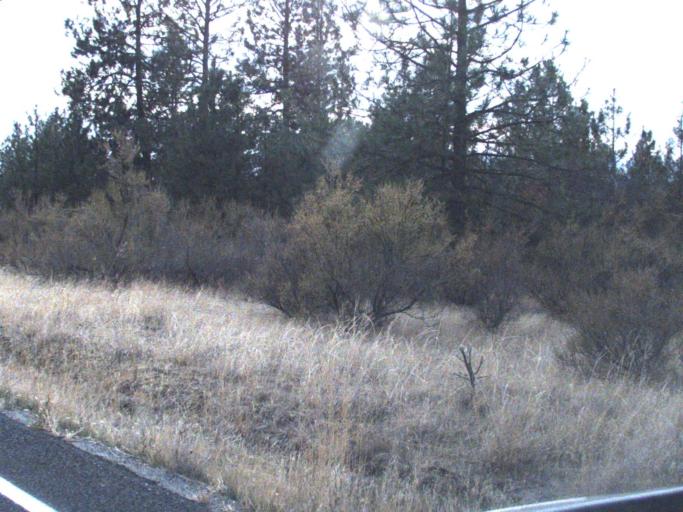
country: US
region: Washington
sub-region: Stevens County
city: Kettle Falls
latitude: 48.1710
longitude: -118.1693
